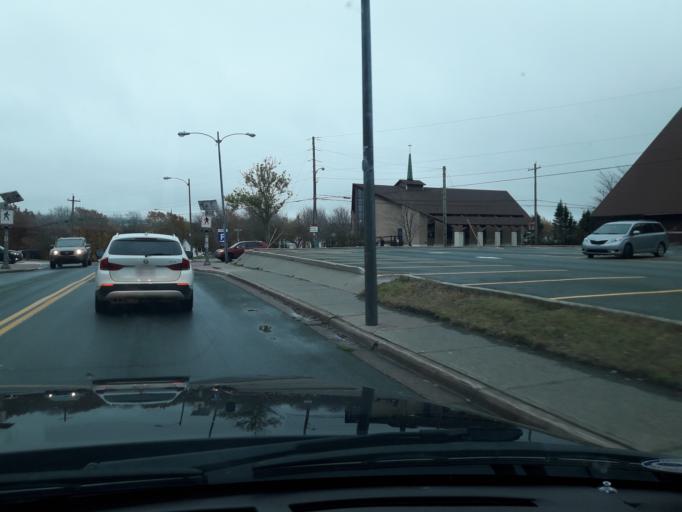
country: CA
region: Newfoundland and Labrador
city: St. John's
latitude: 47.5696
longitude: -52.7353
